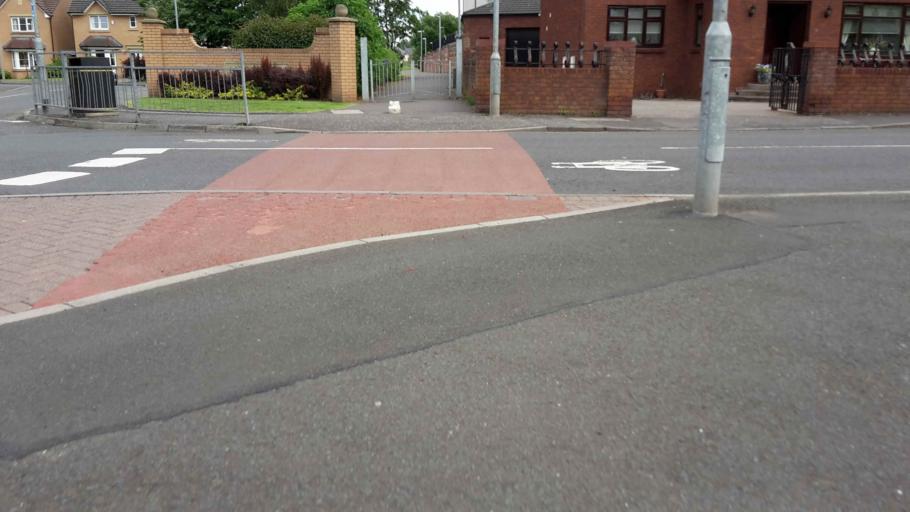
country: GB
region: Scotland
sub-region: South Lanarkshire
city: Uddingston
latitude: 55.8217
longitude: -4.0760
